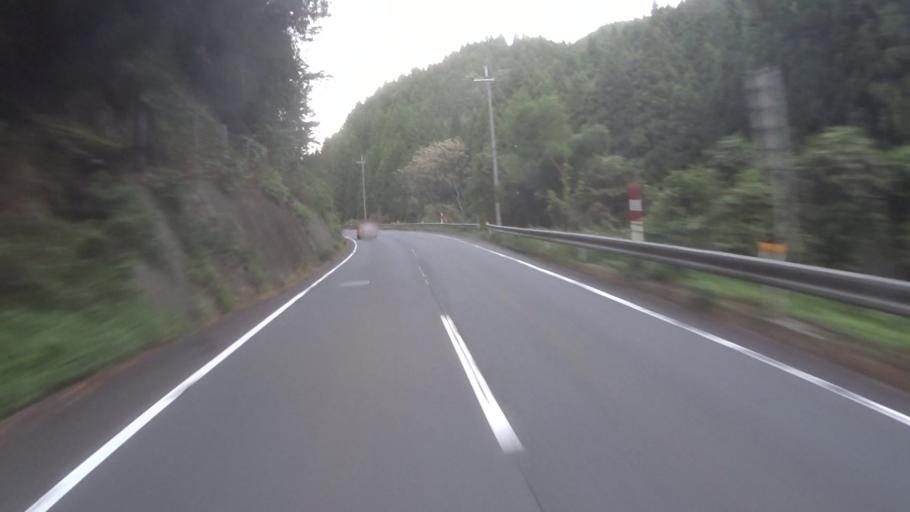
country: JP
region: Kyoto
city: Ayabe
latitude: 35.2410
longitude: 135.3042
